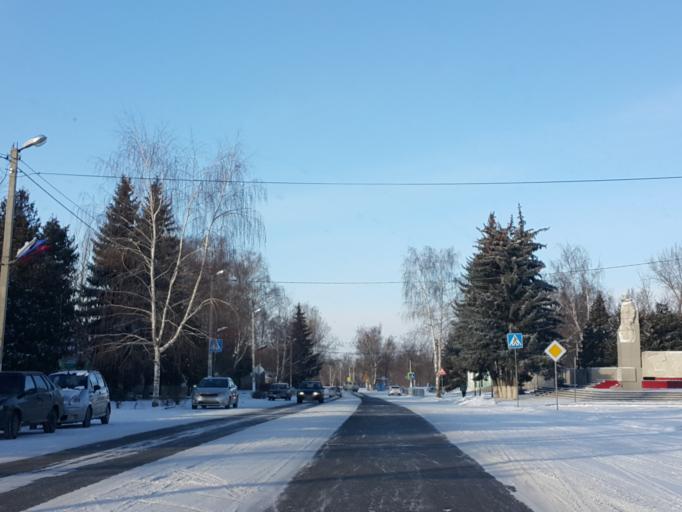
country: RU
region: Tambov
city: Znamenka
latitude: 52.4155
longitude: 41.4411
